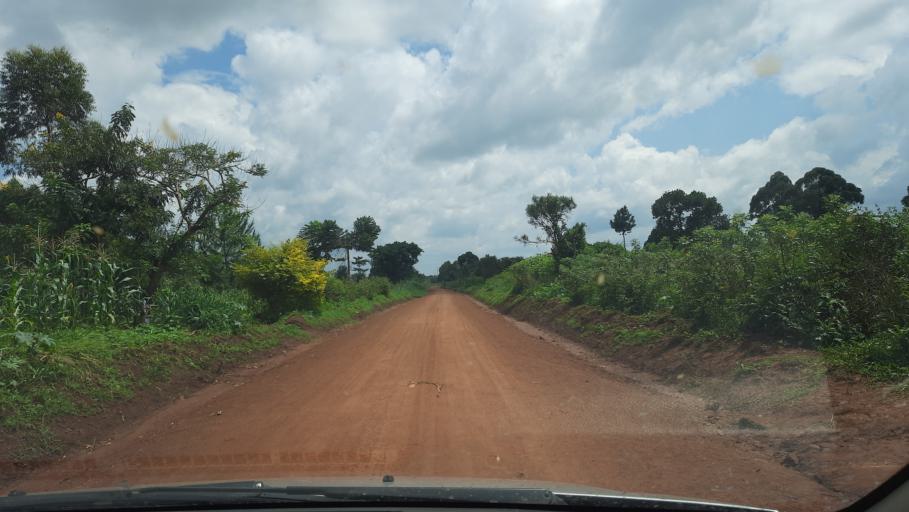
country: UG
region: Western Region
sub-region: Kiryandongo District
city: Kiryandongo
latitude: 1.8187
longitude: 31.9866
